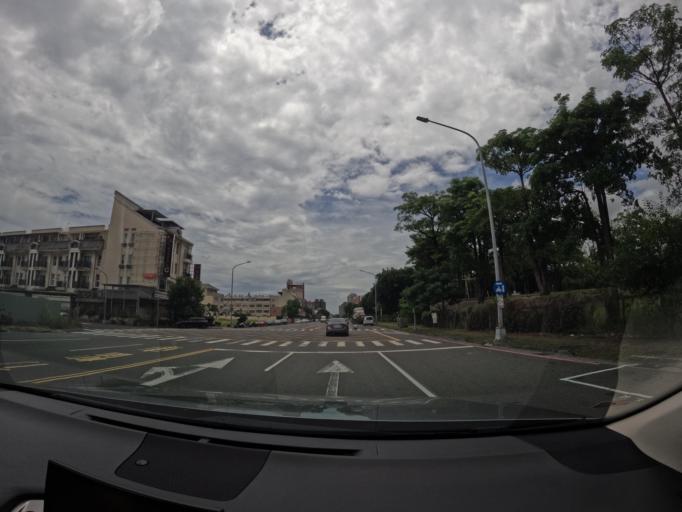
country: TW
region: Kaohsiung
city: Kaohsiung
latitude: 22.7269
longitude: 120.2939
